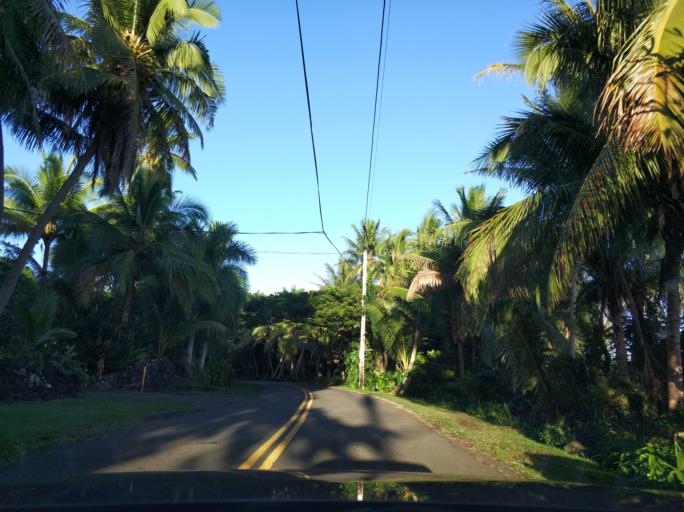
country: US
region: Hawaii
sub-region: Hawaii County
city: Leilani Estates
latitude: 19.3614
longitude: -154.9701
